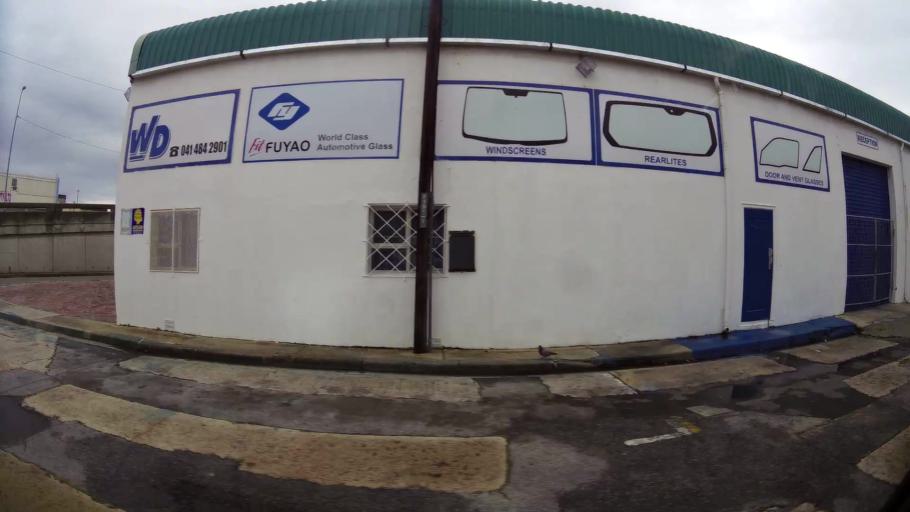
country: ZA
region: Eastern Cape
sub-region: Nelson Mandela Bay Metropolitan Municipality
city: Port Elizabeth
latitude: -33.9509
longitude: 25.6104
